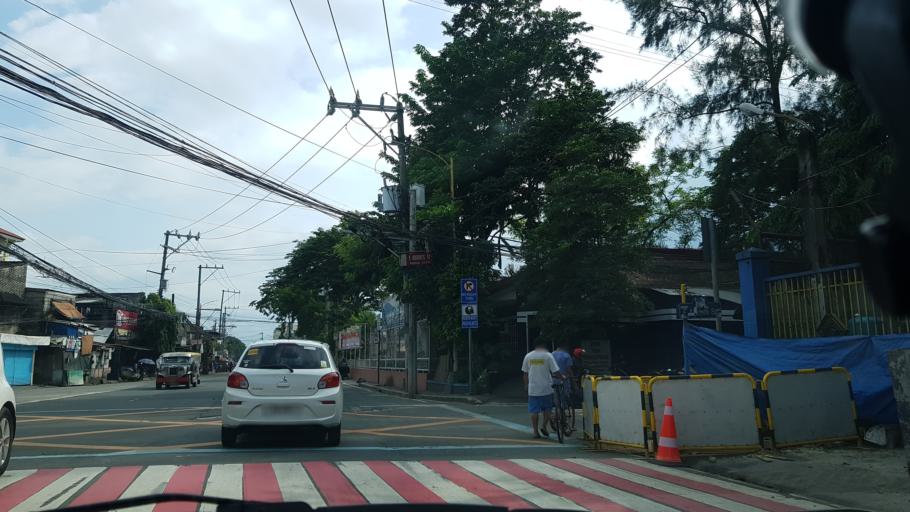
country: PH
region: Metro Manila
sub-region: Pasig
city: Pasig City
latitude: 14.5885
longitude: 121.0891
